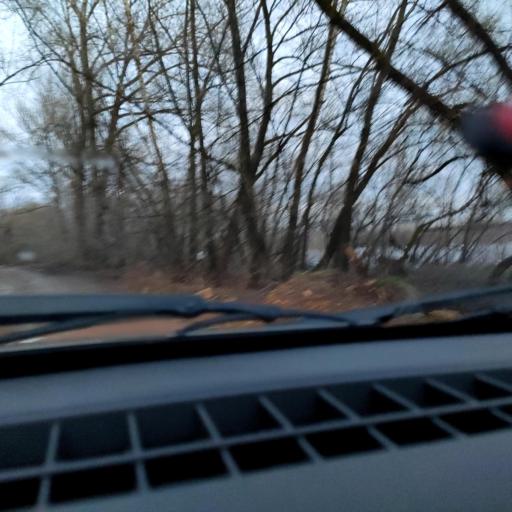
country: RU
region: Bashkortostan
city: Ufa
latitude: 54.6746
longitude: 55.9672
